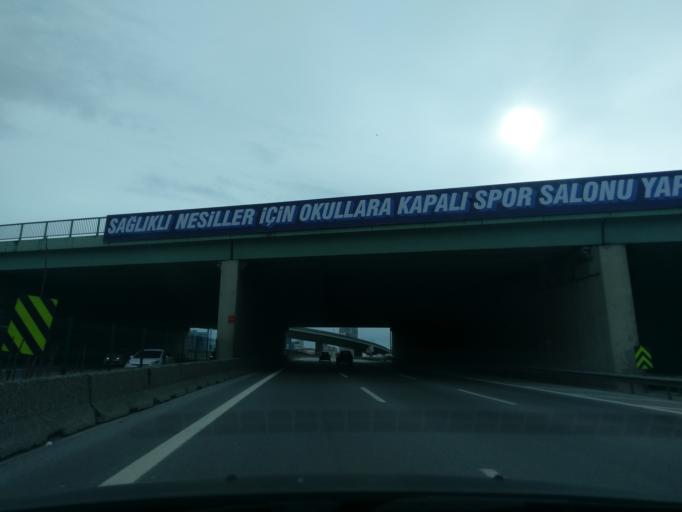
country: TR
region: Istanbul
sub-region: Atasehir
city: Atasehir
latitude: 40.9819
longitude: 29.0943
